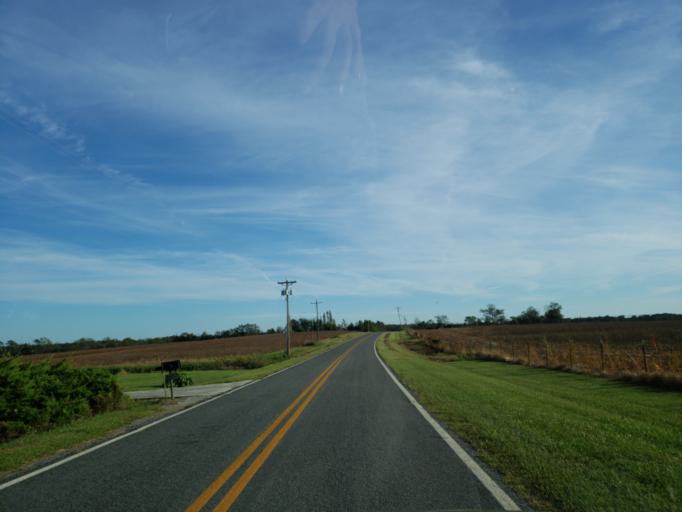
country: US
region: Georgia
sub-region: Dooly County
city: Vienna
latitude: 32.0417
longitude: -83.7542
